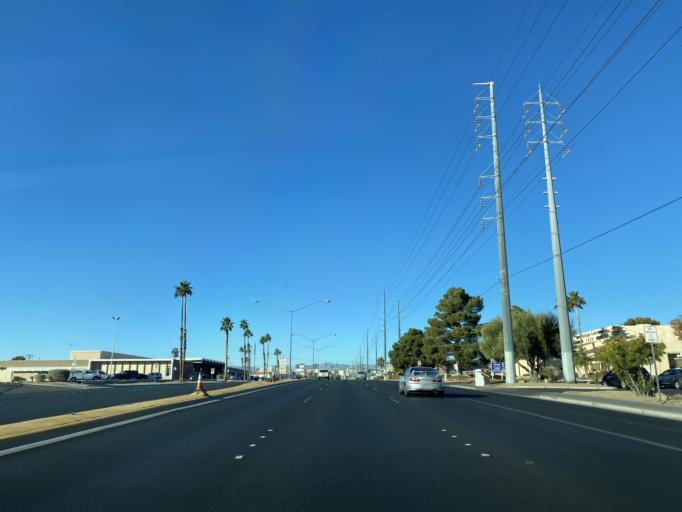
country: US
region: Nevada
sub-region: Clark County
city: Winchester
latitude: 36.1151
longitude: -115.1103
